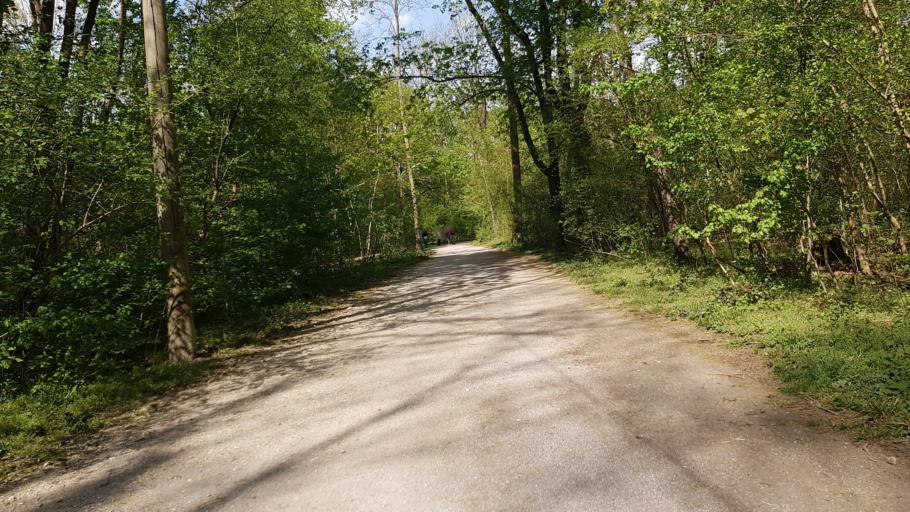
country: DE
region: Bavaria
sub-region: Upper Bavaria
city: Pasing
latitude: 48.1735
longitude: 11.4939
